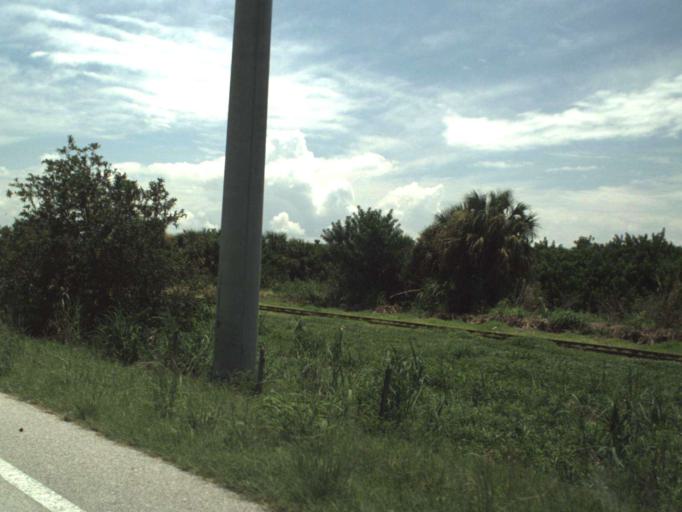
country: US
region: Florida
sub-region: Palm Beach County
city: Pahokee
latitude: 26.9063
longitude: -80.6118
